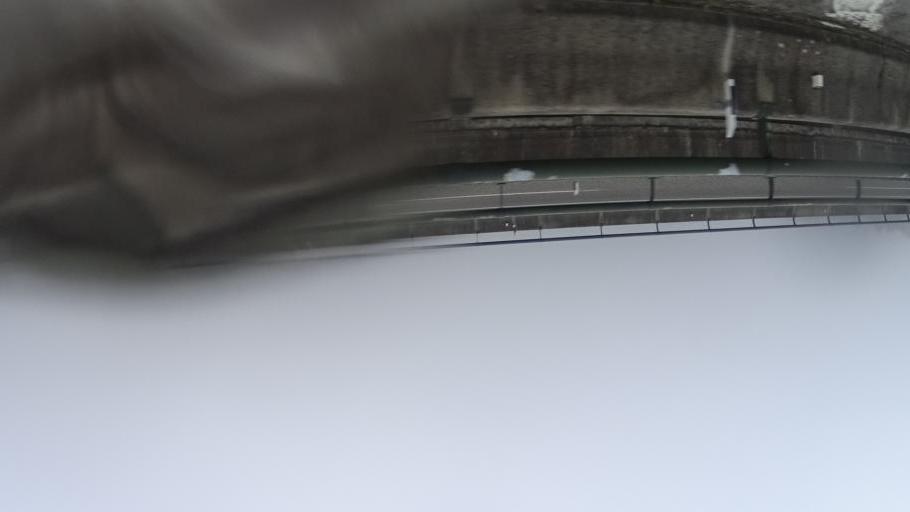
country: ES
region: Galicia
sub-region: Provincia de Lugo
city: Becerrea
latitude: 42.8193
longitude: -7.1084
